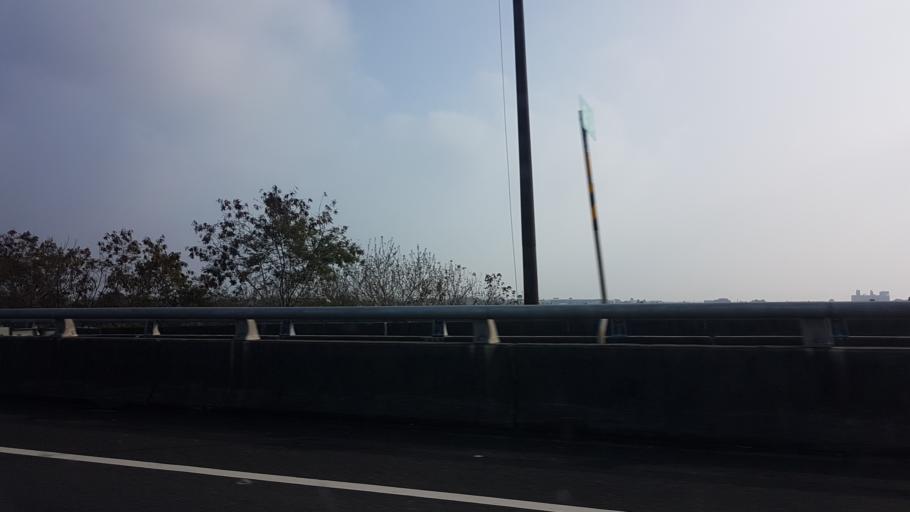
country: TW
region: Taiwan
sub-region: Chiayi
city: Taibao
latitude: 23.4235
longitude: 120.3611
